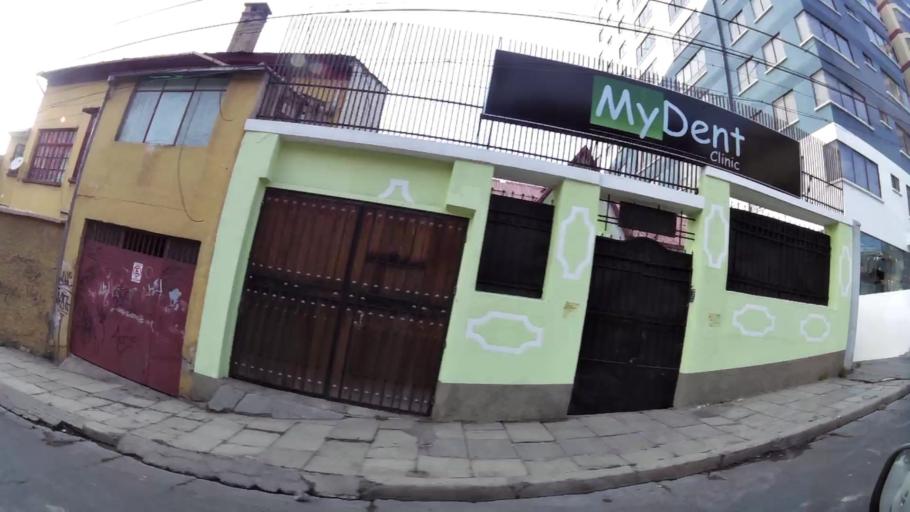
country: BO
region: La Paz
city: La Paz
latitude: -16.5122
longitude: -68.1291
